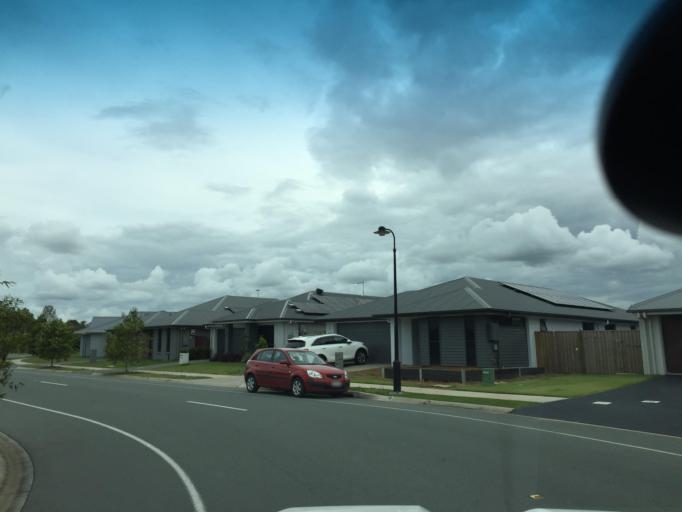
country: AU
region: Queensland
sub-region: Moreton Bay
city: Caboolture
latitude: -27.0647
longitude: 152.9334
